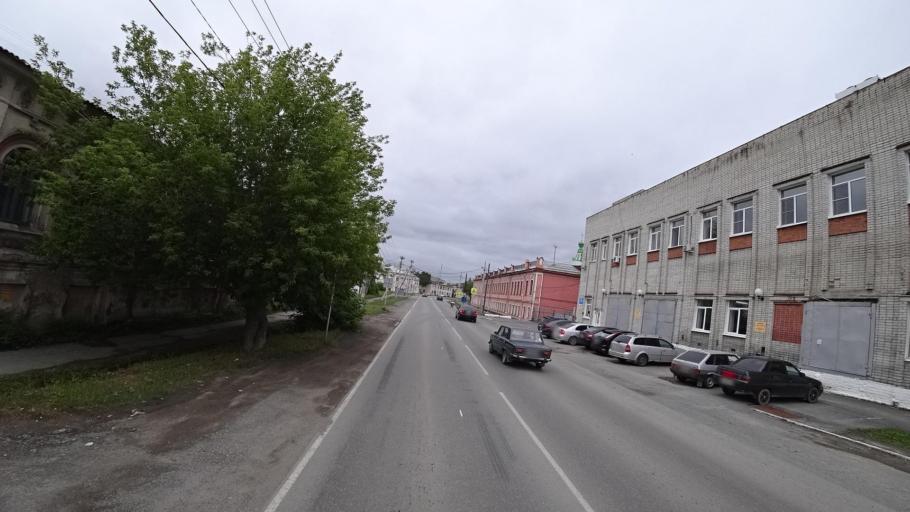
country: RU
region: Sverdlovsk
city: Kamyshlov
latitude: 56.8445
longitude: 62.7007
